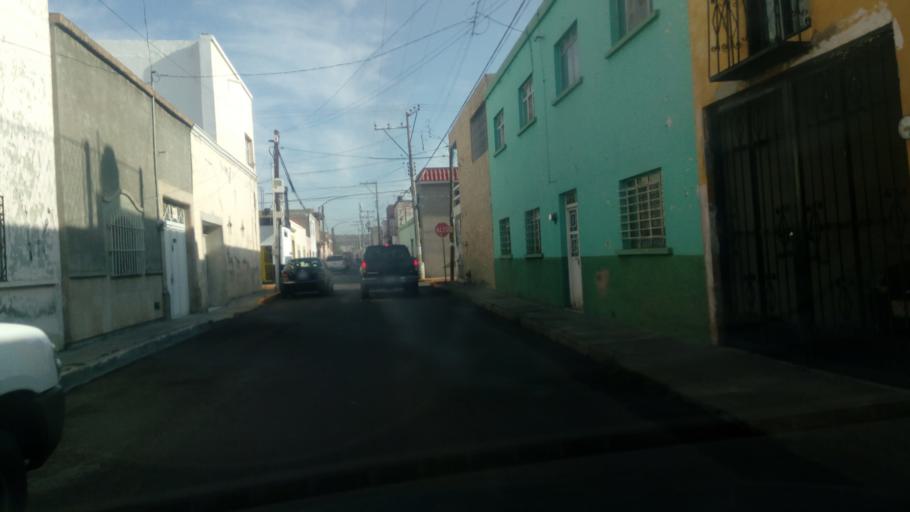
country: MX
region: Durango
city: Victoria de Durango
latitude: 24.0317
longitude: -104.6642
